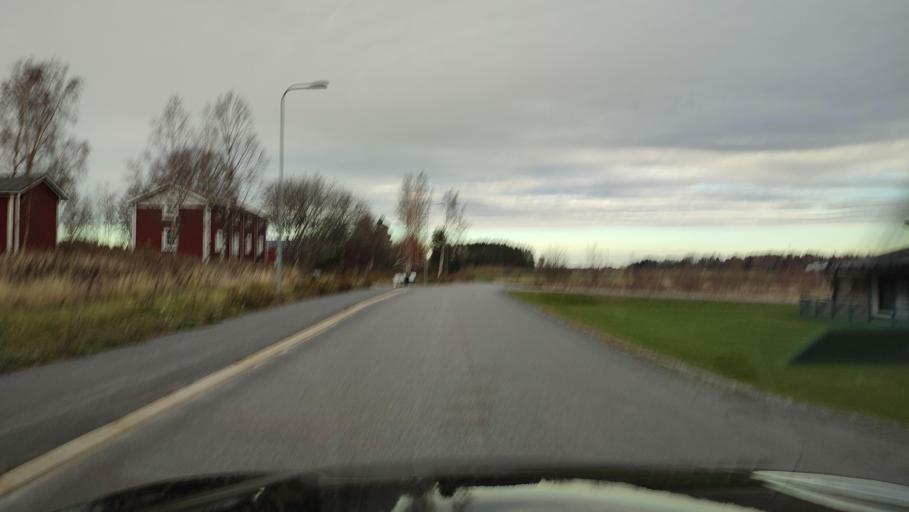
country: FI
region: Ostrobothnia
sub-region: Sydosterbotten
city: Naerpes
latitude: 62.4770
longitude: 21.3245
